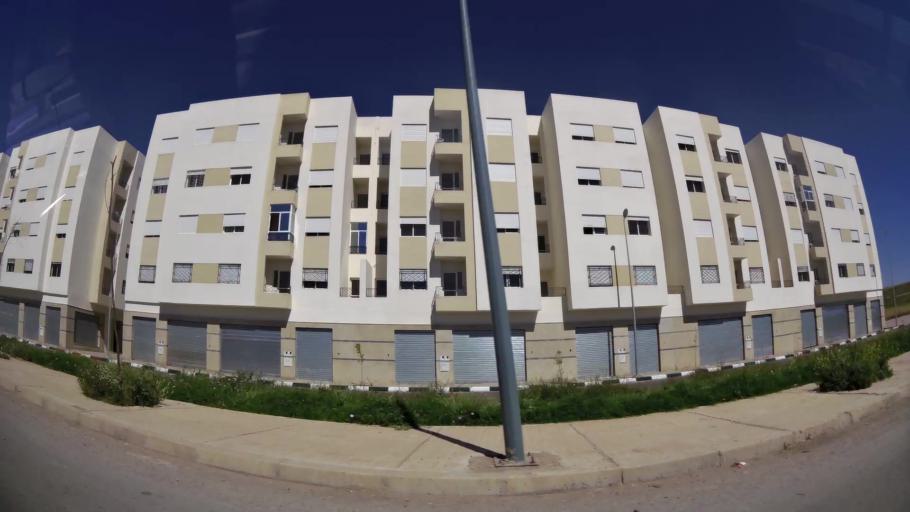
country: MA
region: Oriental
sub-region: Oujda-Angad
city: Oujda
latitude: 34.6712
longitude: -1.8596
